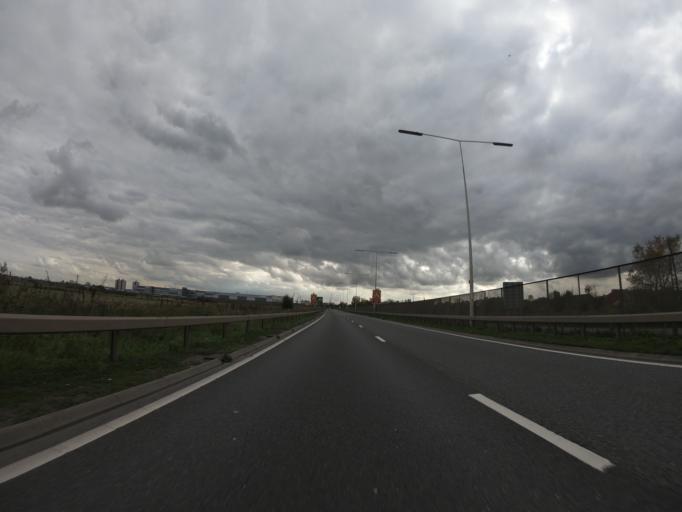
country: GB
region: England
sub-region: Borough of Thurrock
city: Tilbury
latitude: 51.4741
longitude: 0.3483
